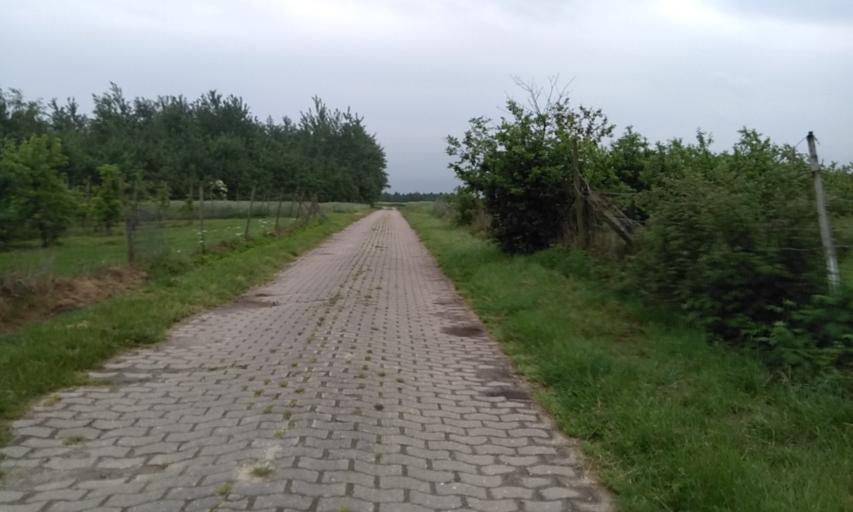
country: DE
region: Lower Saxony
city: Buxtehude
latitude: 53.4637
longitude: 9.6450
